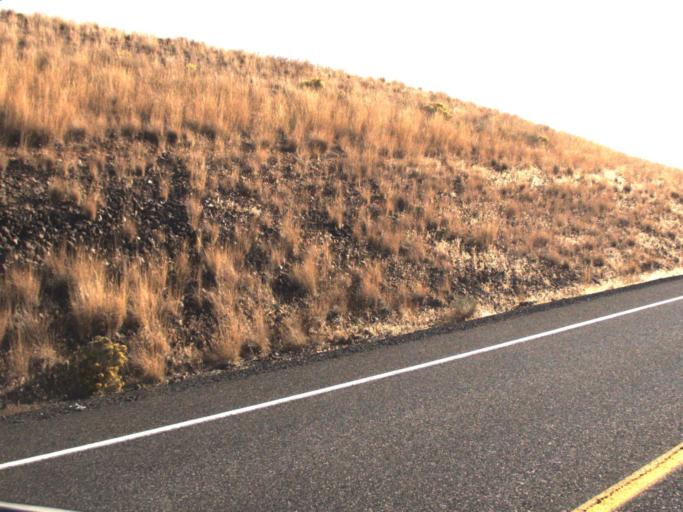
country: US
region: Washington
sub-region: Benton County
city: Highland
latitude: 46.1507
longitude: -119.1793
